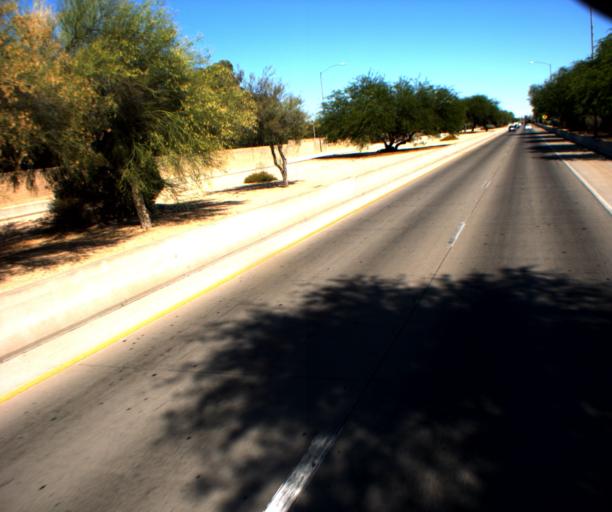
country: US
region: Arizona
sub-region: Pima County
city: Tucson
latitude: 32.2013
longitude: -110.9328
